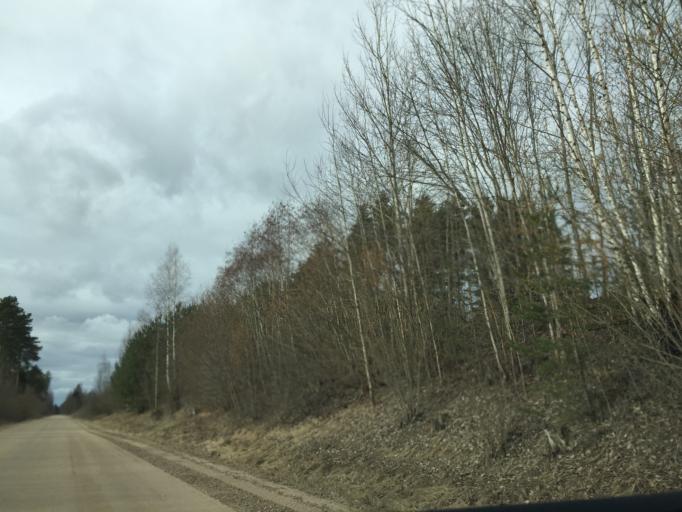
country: LV
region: Daugavpils
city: Daugavpils
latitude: 55.9573
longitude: 26.6909
